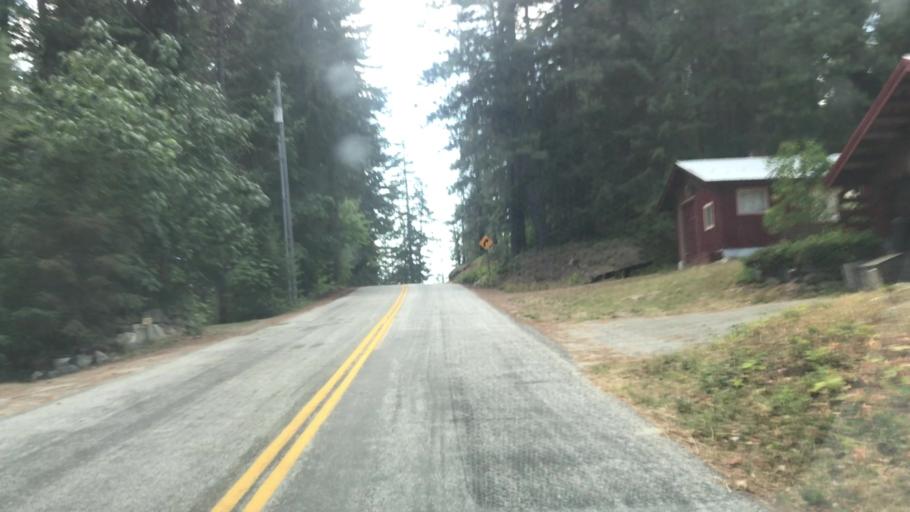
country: US
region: Washington
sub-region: Chelan County
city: Leavenworth
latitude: 47.8309
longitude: -120.7784
